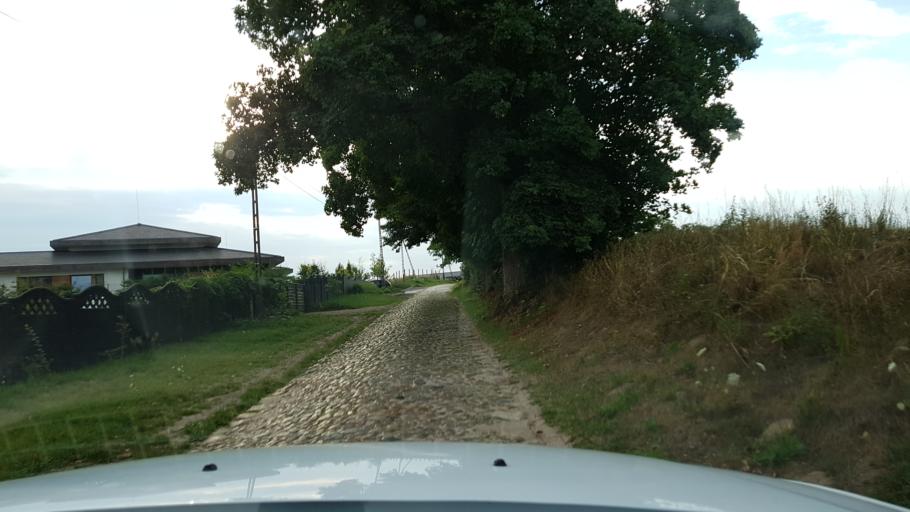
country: PL
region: West Pomeranian Voivodeship
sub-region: Powiat swidwinski
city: Polczyn-Zdroj
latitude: 53.7802
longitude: 16.0907
